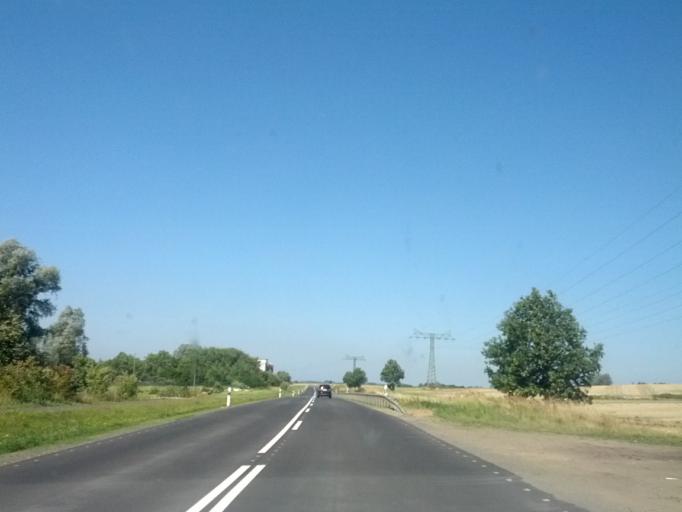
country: DE
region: Mecklenburg-Vorpommern
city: Sagard
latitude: 54.5009
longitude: 13.5615
